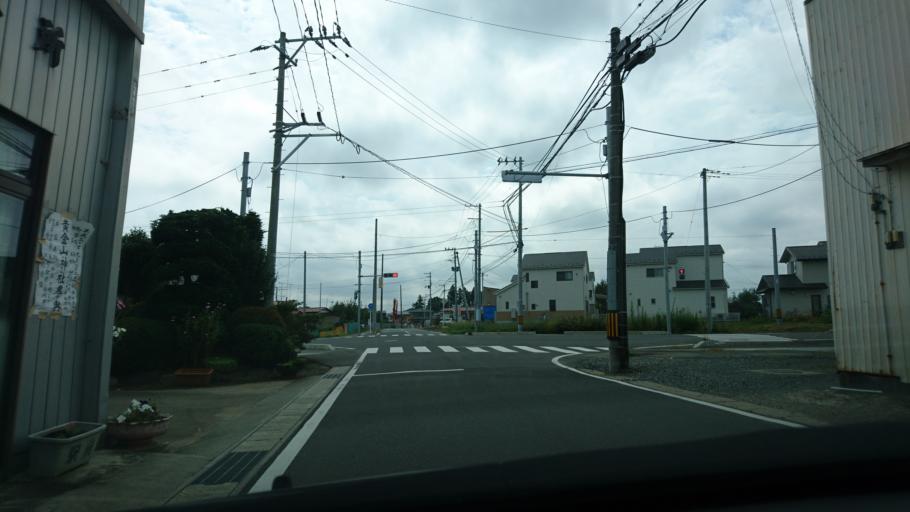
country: JP
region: Miyagi
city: Furukawa
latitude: 38.7313
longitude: 141.0299
